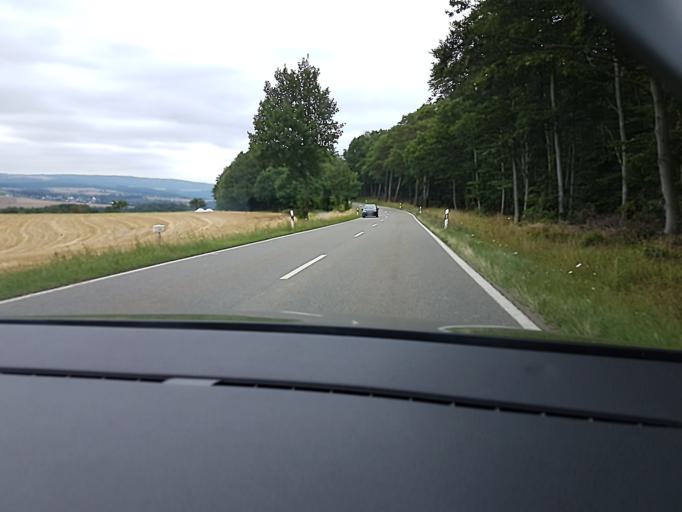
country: DE
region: Rheinland-Pfalz
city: Bornich
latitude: 50.1382
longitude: 7.7512
